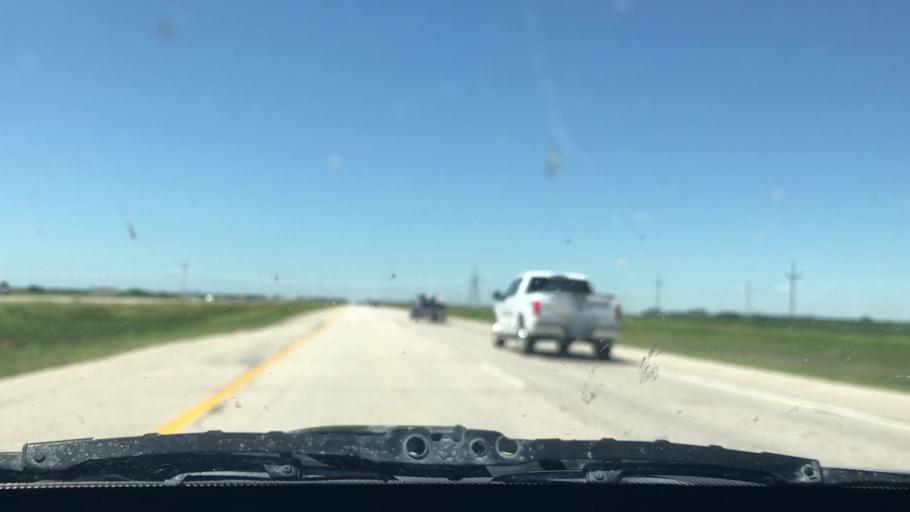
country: CA
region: Manitoba
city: Steinbach
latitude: 49.7085
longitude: -96.6641
